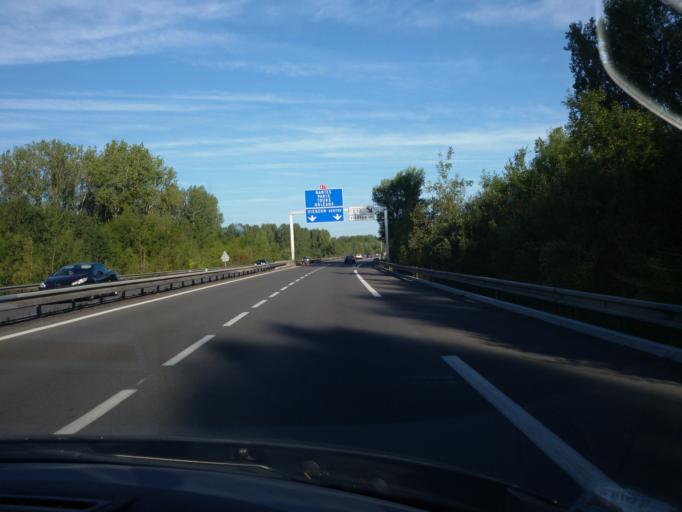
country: FR
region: Centre
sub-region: Departement du Cher
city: Vierzon
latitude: 47.2048
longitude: 2.1253
